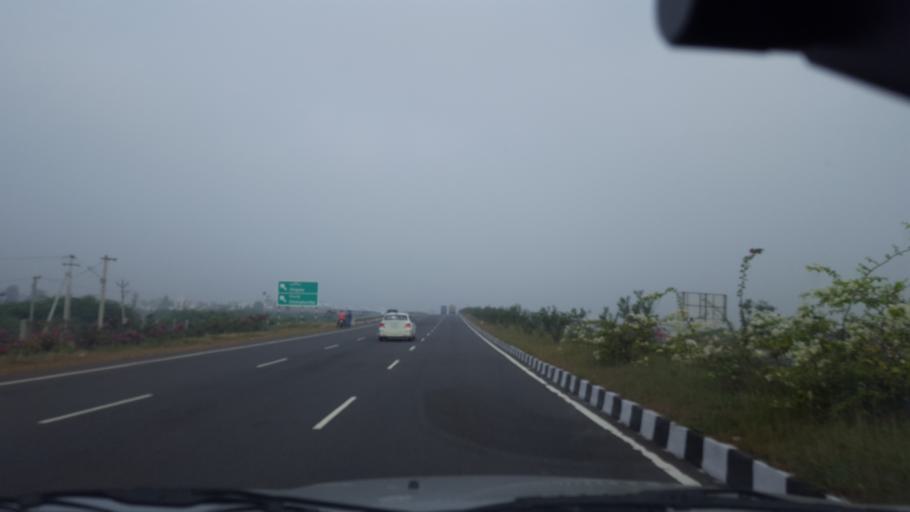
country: IN
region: Andhra Pradesh
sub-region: Prakasam
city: Ongole
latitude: 15.5260
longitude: 80.0595
